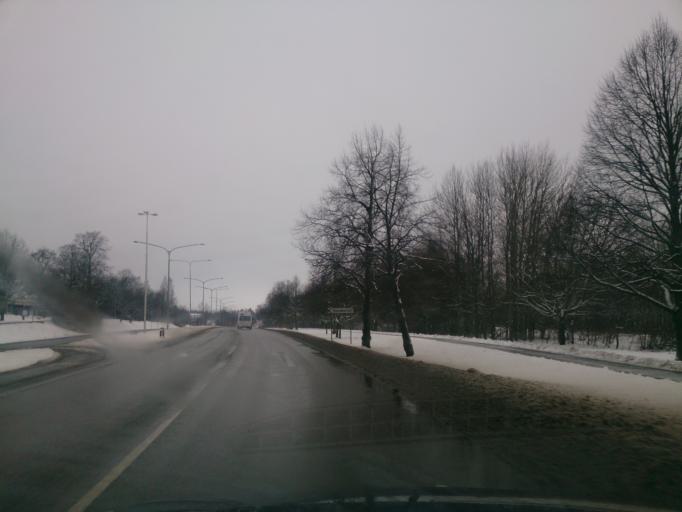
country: SE
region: OEstergoetland
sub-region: Norrkopings Kommun
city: Norrkoping
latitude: 58.6062
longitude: 16.1651
